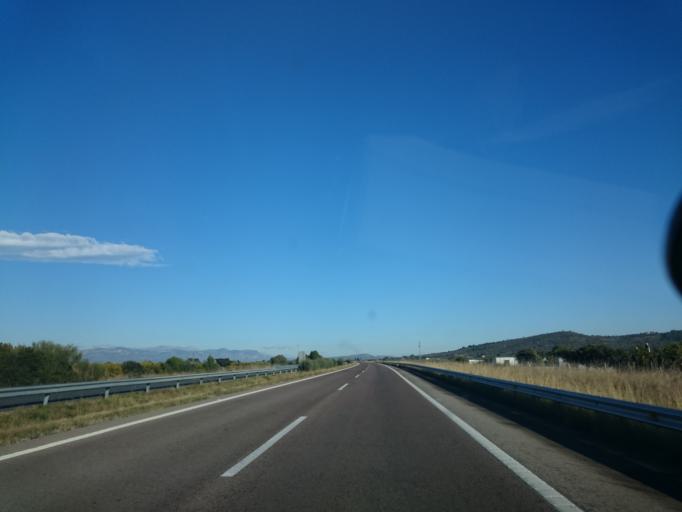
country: ES
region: Valencia
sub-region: Provincia de Castello
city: Vinaros
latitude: 40.4960
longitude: 0.4155
